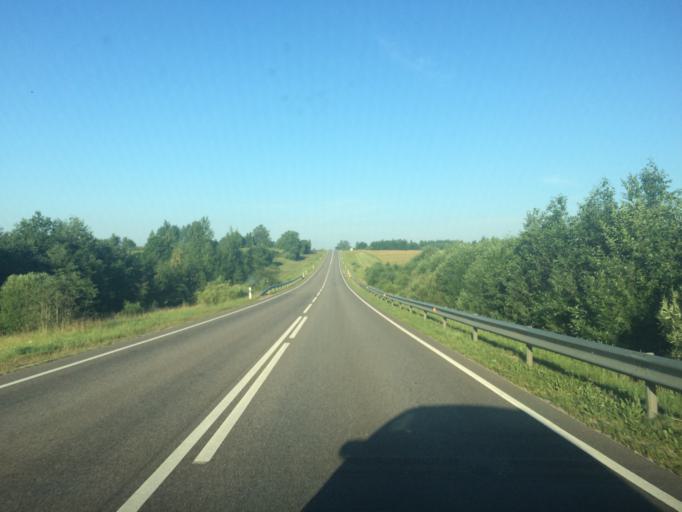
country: LT
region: Utenos apskritis
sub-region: Anyksciai
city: Anyksciai
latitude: 55.3870
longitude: 25.0546
